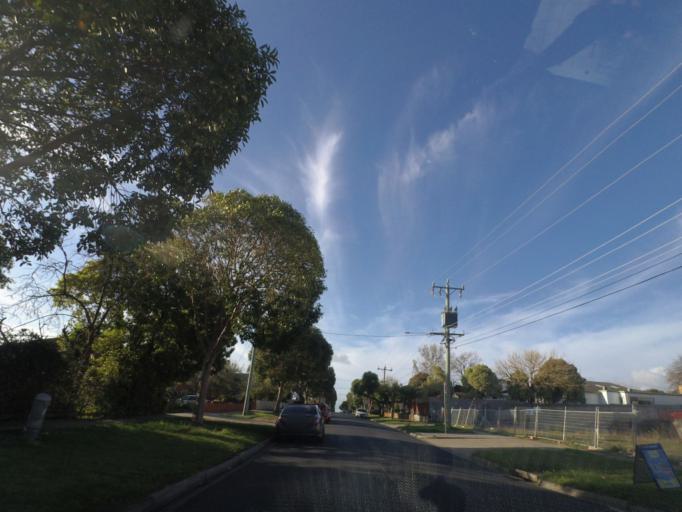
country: AU
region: Victoria
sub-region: Whitehorse
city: Box Hill North
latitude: -37.8062
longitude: 145.1330
